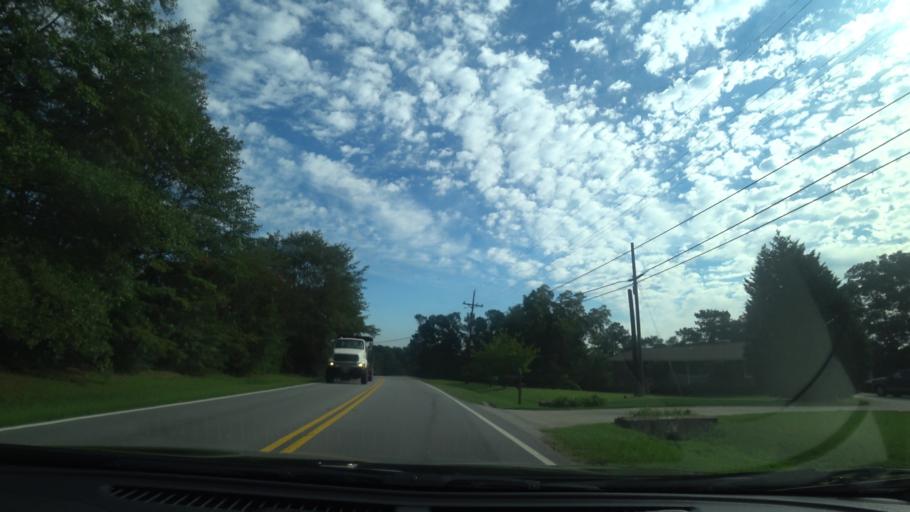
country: US
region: Georgia
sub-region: Rockdale County
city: Lakeview Estates
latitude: 33.7548
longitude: -83.9834
